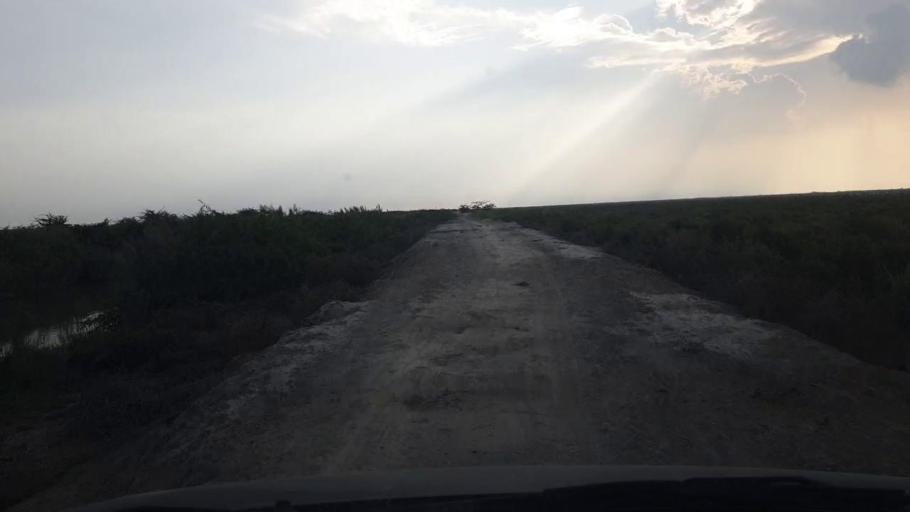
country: PK
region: Sindh
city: Badin
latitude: 24.4557
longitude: 68.6863
